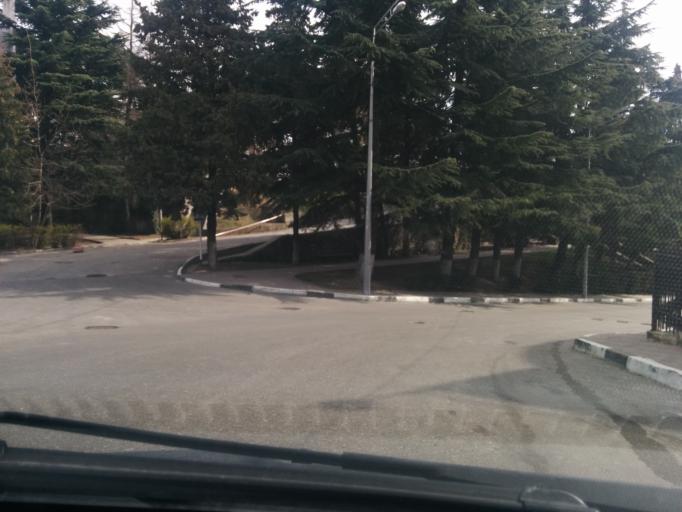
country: RU
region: Krasnodarskiy
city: Tuapse
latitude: 44.1014
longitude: 39.0780
